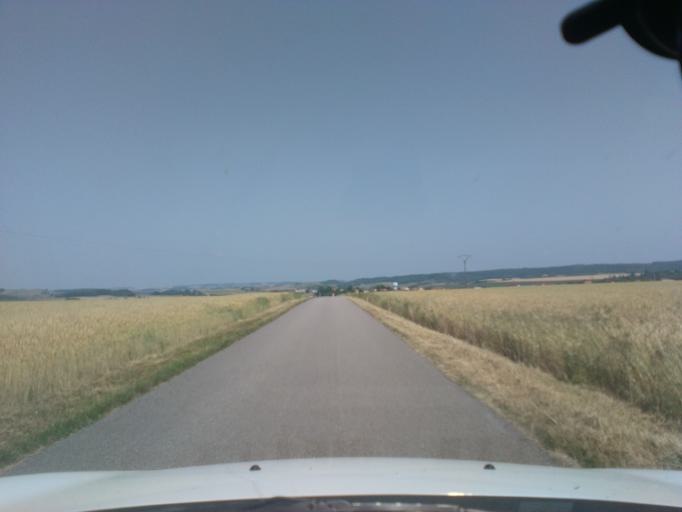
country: FR
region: Lorraine
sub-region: Departement des Vosges
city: Mirecourt
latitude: 48.3142
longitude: 6.1113
